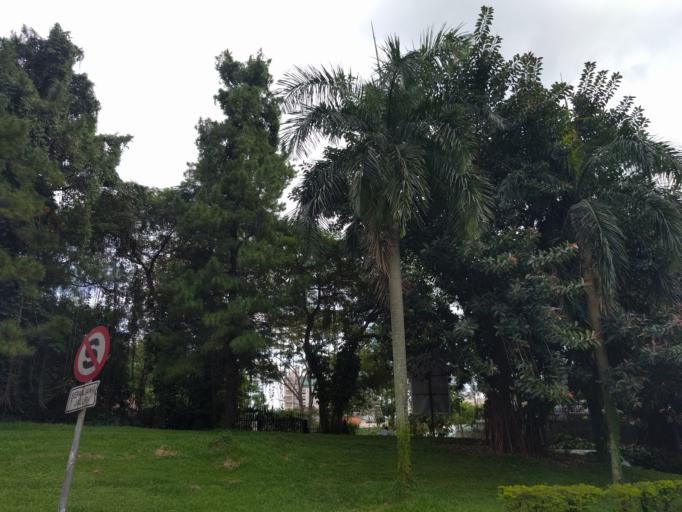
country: ID
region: West Java
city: Bogor
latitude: -6.6041
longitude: 106.8074
